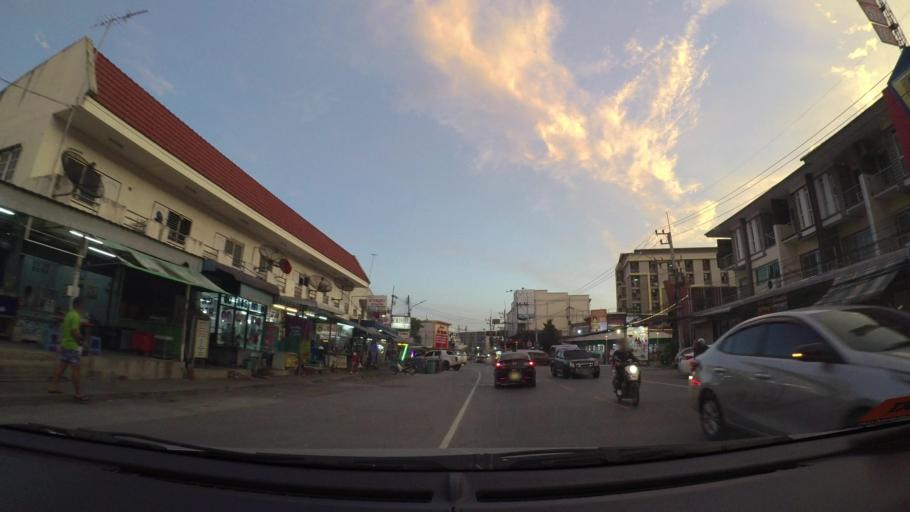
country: TH
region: Chon Buri
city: Chon Buri
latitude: 13.4181
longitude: 101.0000
